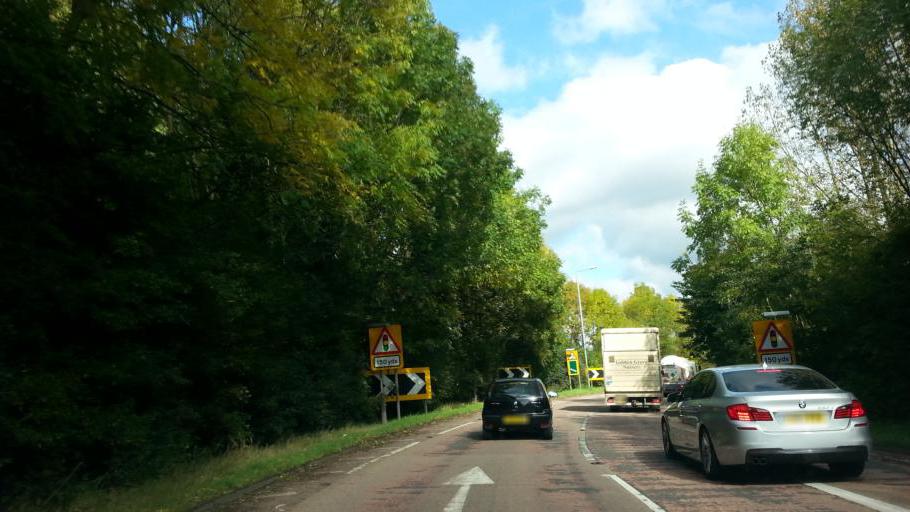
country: GB
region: England
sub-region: Derby
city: Derby
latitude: 52.9201
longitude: -1.5169
